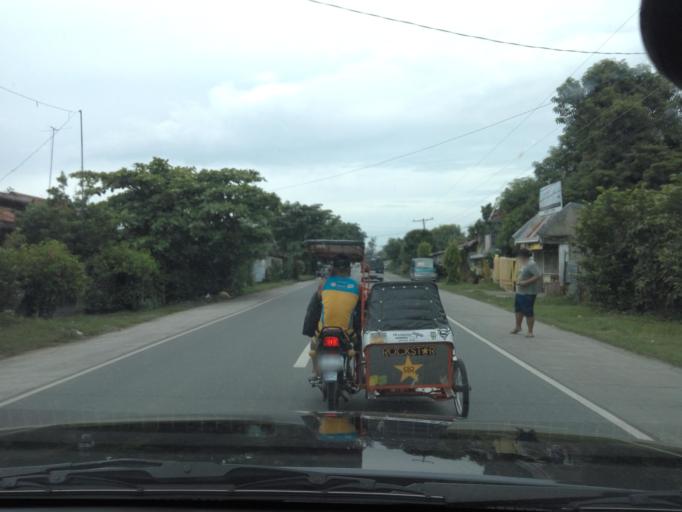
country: PH
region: Central Luzon
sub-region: Province of Nueva Ecija
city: Carmen
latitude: 15.4465
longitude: 120.8232
